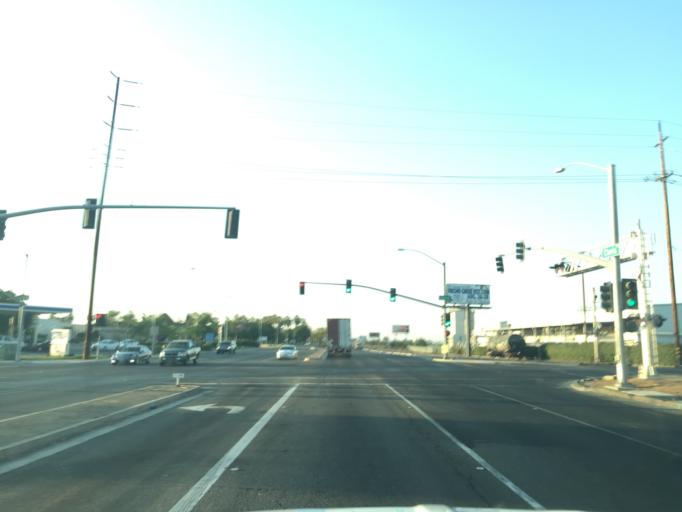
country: US
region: California
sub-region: Fresno County
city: Sunnyside
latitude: 36.7570
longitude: -119.7004
